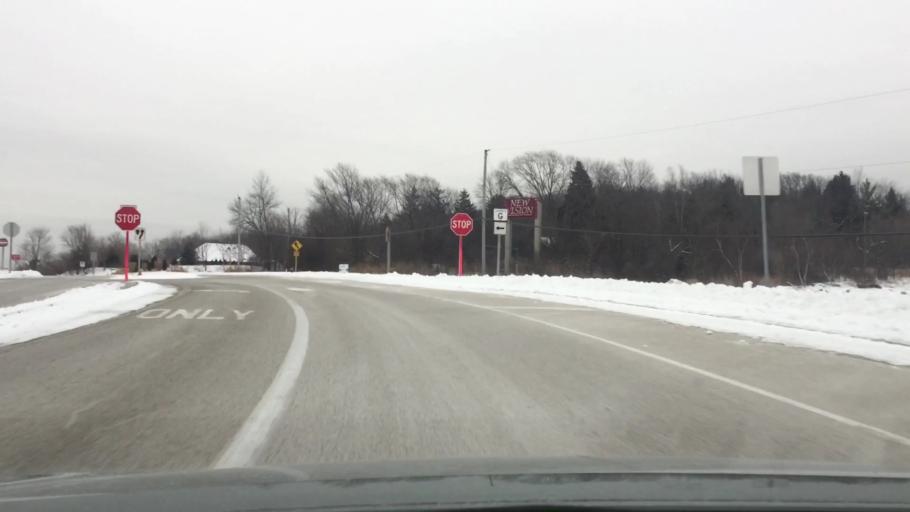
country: US
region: Wisconsin
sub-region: Waukesha County
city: Pewaukee
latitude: 43.0494
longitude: -88.3033
